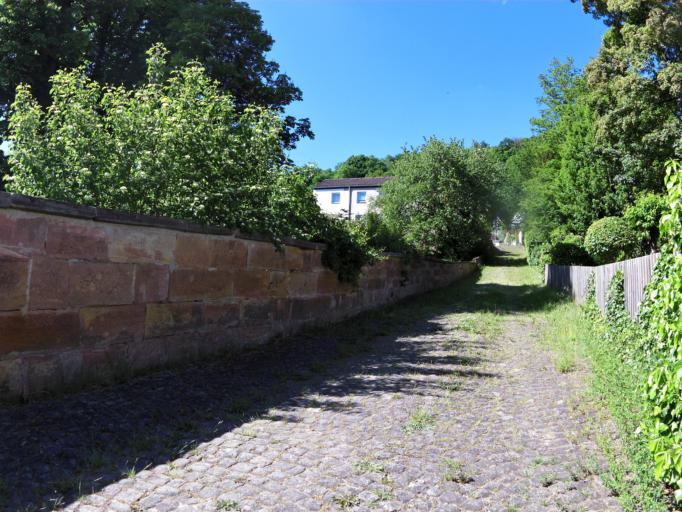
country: DE
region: Hesse
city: Philippsthal
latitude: 50.8420
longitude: 10.0001
